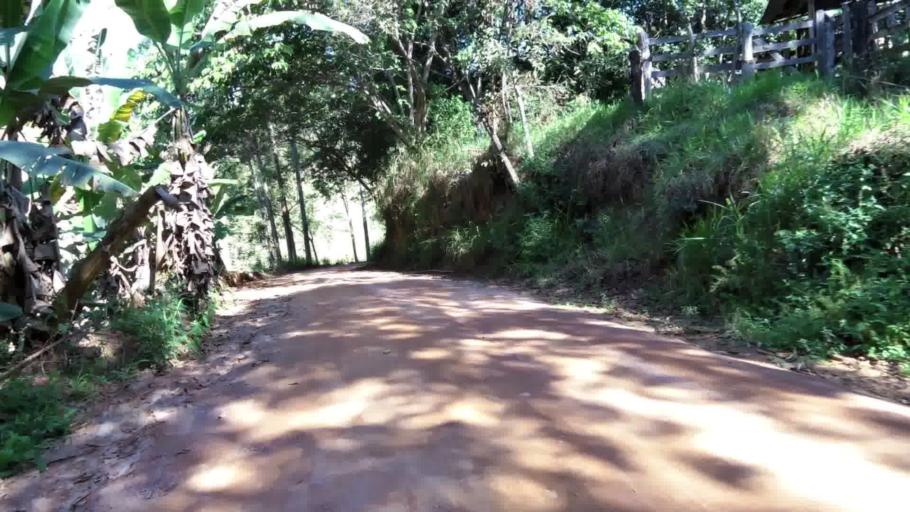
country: BR
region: Espirito Santo
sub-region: Alfredo Chaves
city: Alfredo Chaves
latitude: -20.5704
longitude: -40.7854
